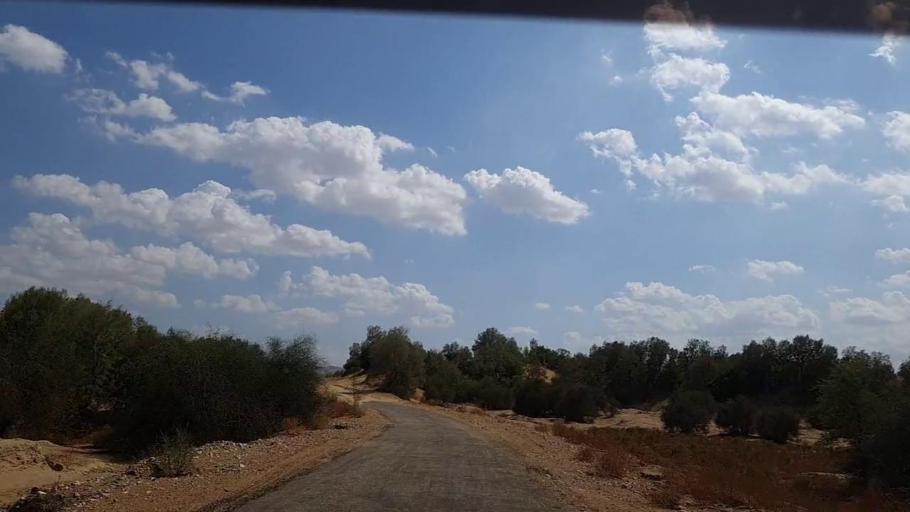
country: PK
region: Sindh
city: Johi
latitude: 26.5174
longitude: 67.4509
